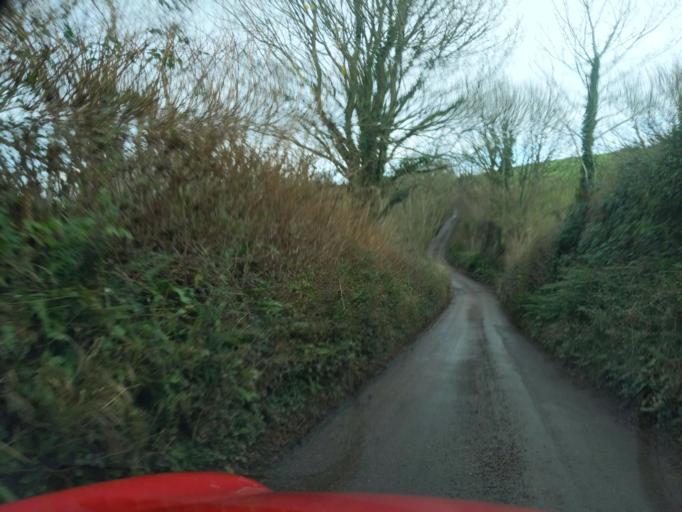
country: GB
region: England
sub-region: Devon
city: Salcombe
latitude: 50.2513
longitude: -3.6721
